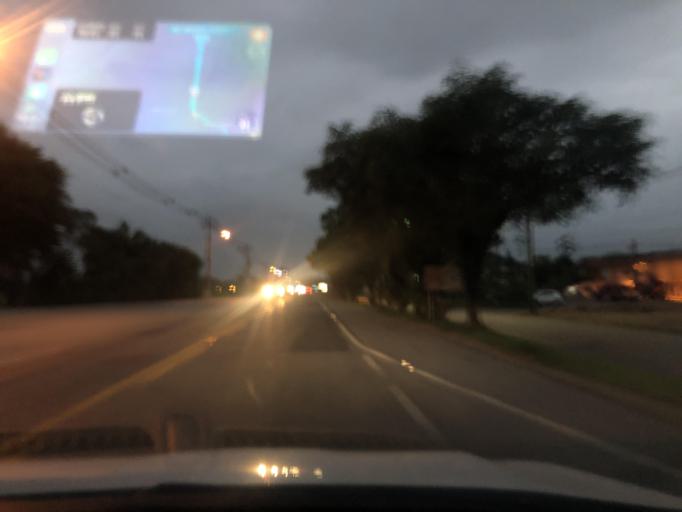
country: BR
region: Santa Catarina
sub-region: Jaragua Do Sul
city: Jaragua do Sul
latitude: -26.6108
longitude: -49.0104
